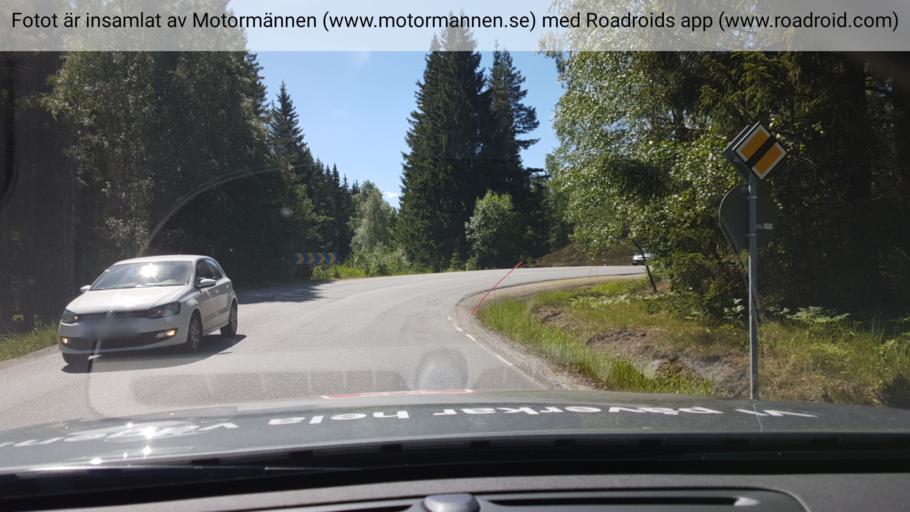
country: SE
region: Stockholm
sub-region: Haninge Kommun
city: Haninge
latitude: 59.1544
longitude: 18.1800
